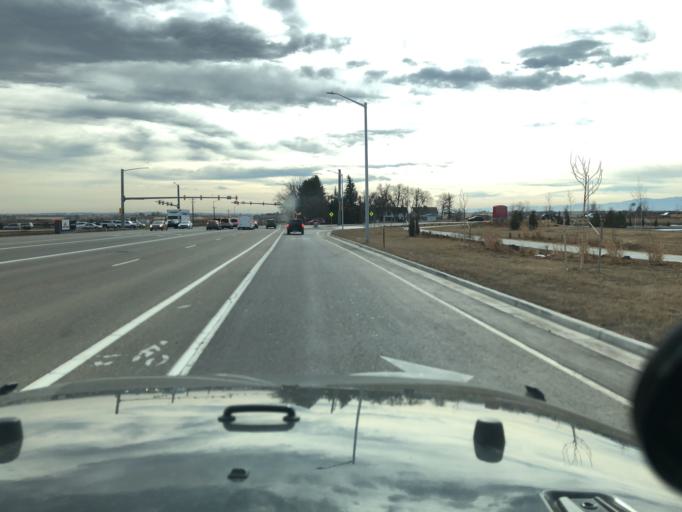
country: US
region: Colorado
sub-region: Boulder County
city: Longmont
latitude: 40.1618
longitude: -105.0555
